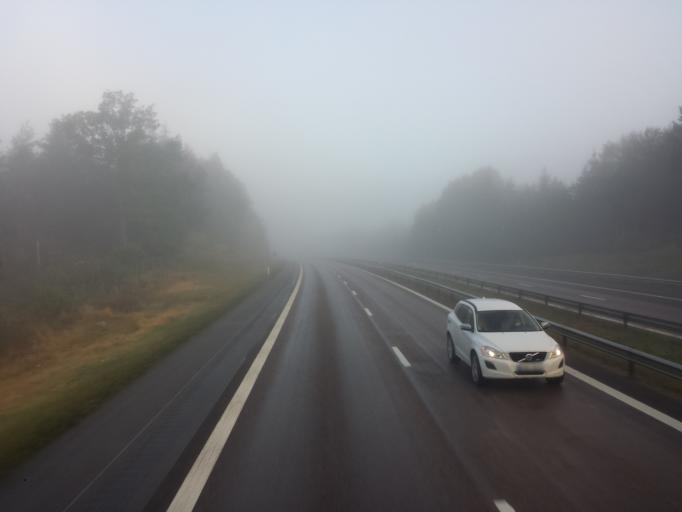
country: SE
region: Halland
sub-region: Kungsbacka Kommun
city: Fjaeras kyrkby
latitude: 57.4253
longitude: 12.1632
